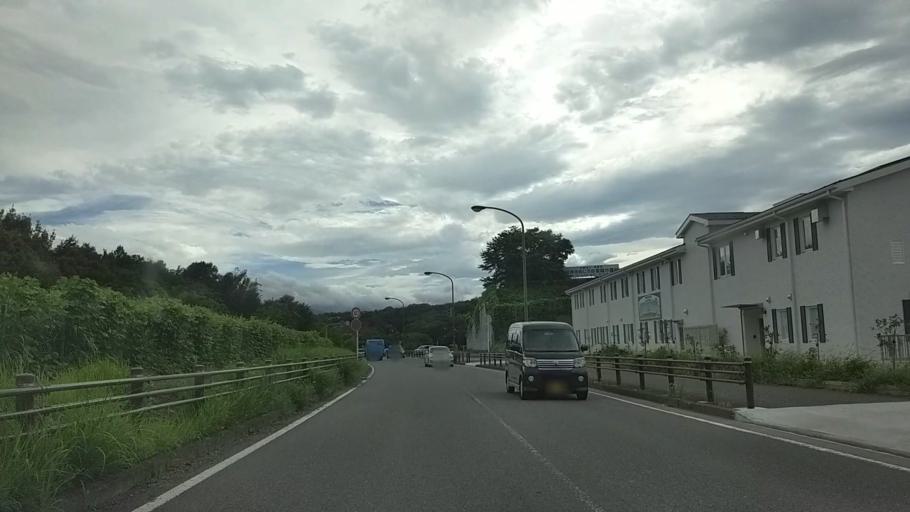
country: JP
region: Tokyo
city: Hachioji
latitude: 35.6311
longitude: 139.3172
